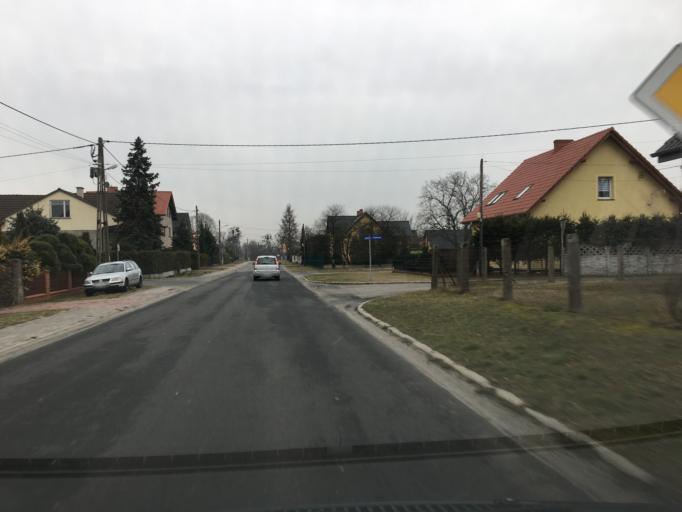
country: PL
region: Opole Voivodeship
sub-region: Powiat kedzierzynsko-kozielski
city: Bierawa
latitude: 50.2863
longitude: 18.2382
